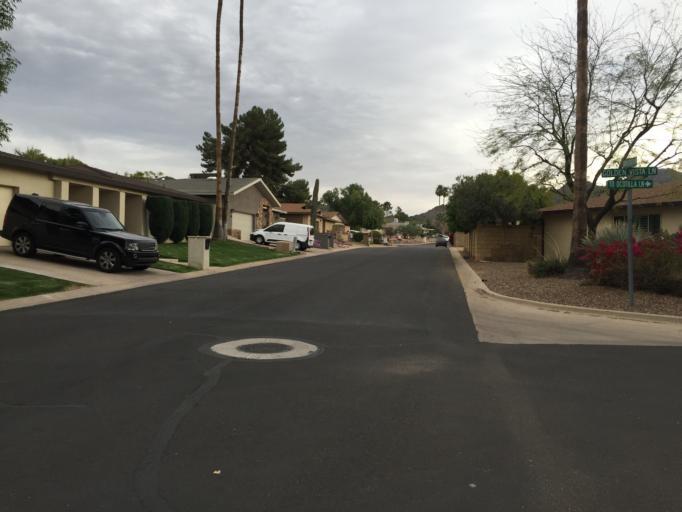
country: US
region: Arizona
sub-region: Maricopa County
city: Paradise Valley
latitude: 33.5719
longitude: -112.0163
